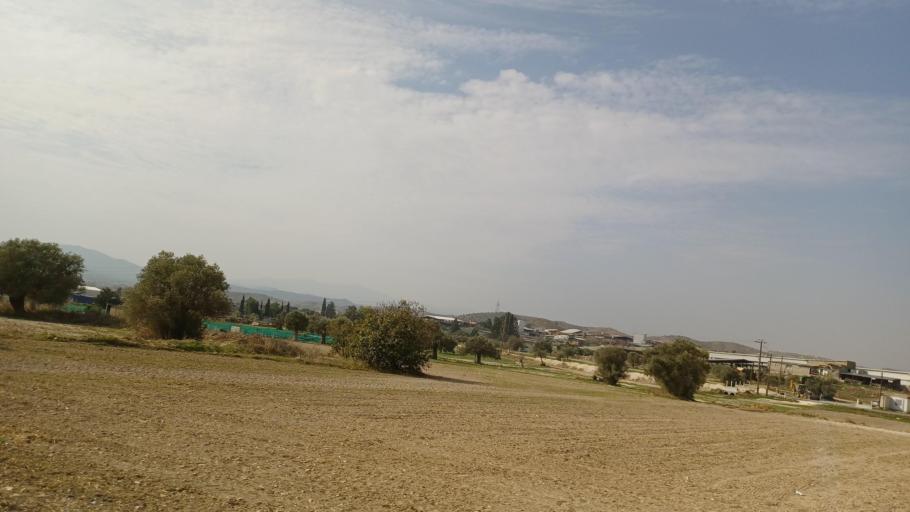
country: CY
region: Lefkosia
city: Lympia
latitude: 34.9871
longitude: 33.4547
